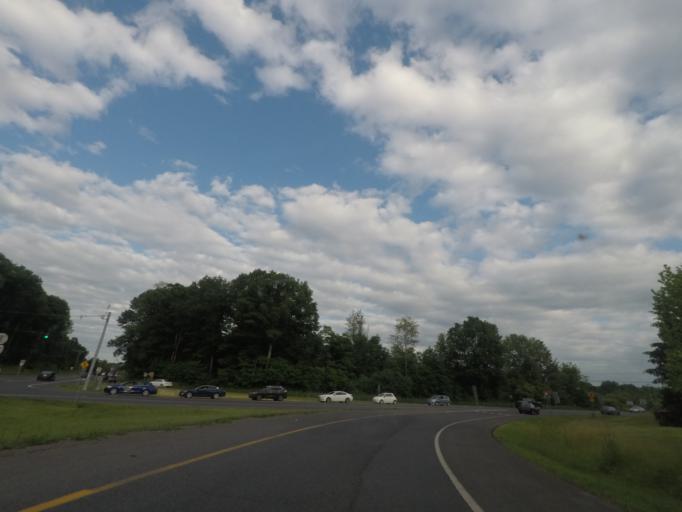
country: US
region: New York
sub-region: Ulster County
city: New Paltz
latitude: 41.7410
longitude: -74.0621
